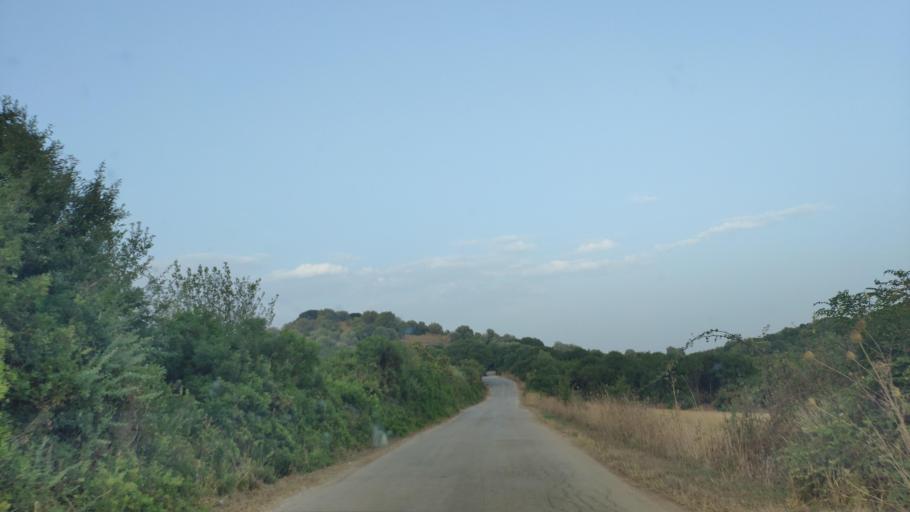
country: GR
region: West Greece
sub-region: Nomos Aitolias kai Akarnanias
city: Monastirakion
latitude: 38.9166
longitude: 20.9728
